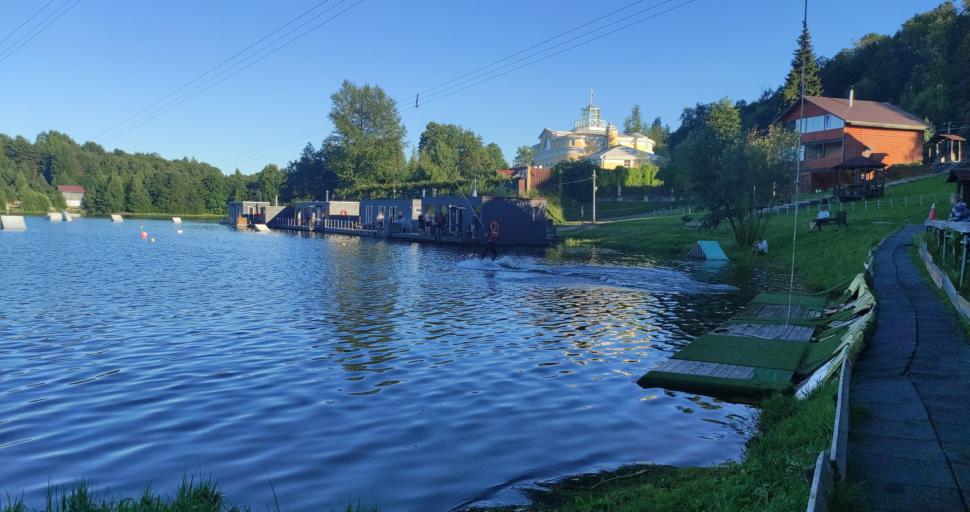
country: RU
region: Leningrad
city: Toksovo
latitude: 60.1556
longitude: 30.5536
